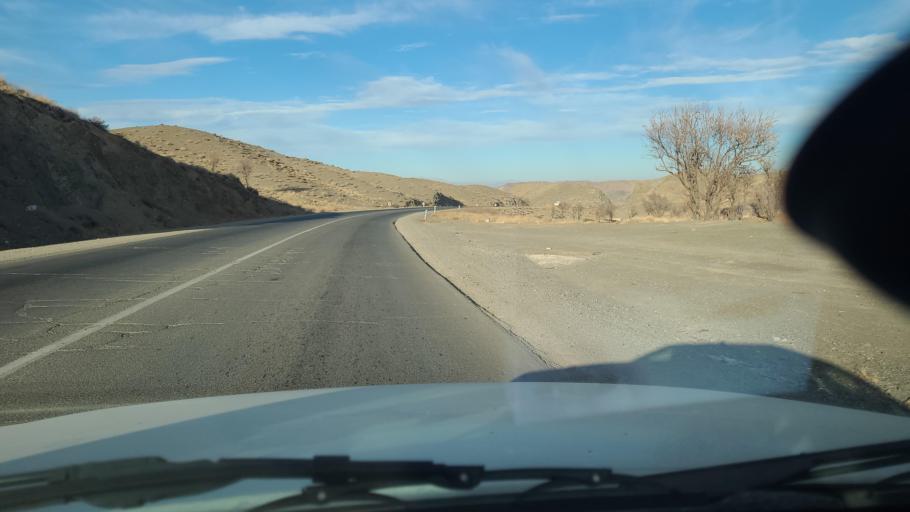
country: IR
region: Razavi Khorasan
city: Sabzevar
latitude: 36.4146
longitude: 57.5515
